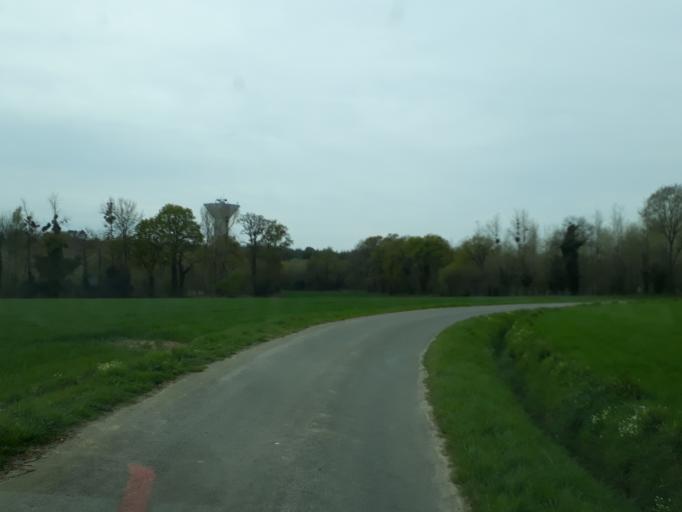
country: FR
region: Brittany
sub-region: Departement du Morbihan
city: Sulniac
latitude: 47.6823
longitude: -2.5846
